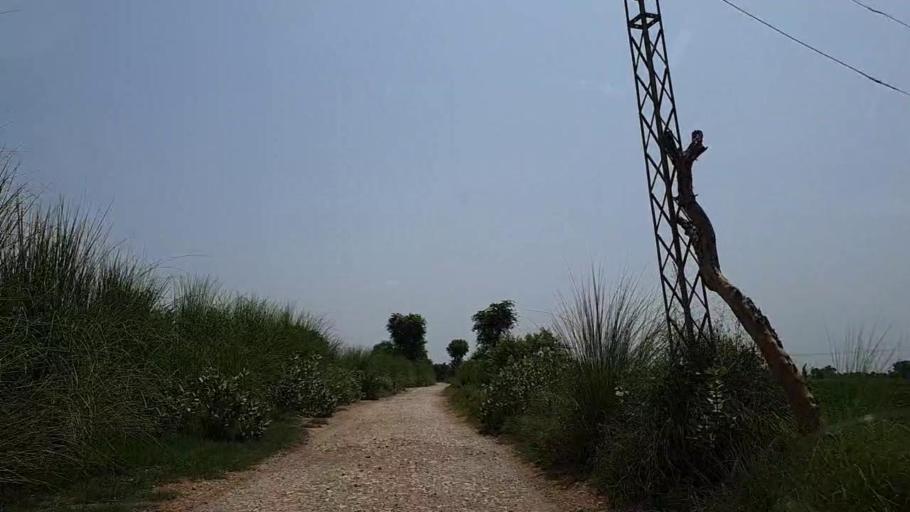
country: PK
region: Sindh
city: Adilpur
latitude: 27.9367
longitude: 69.3942
